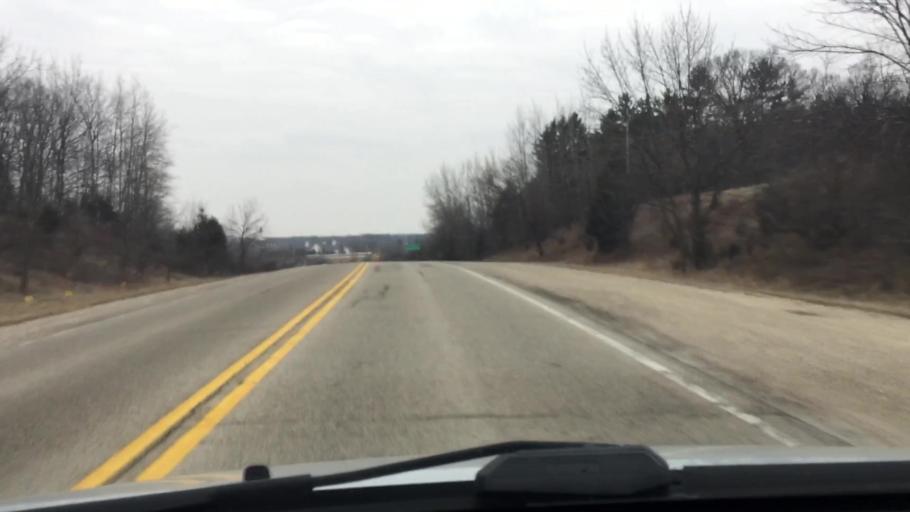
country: US
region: Wisconsin
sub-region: Waukesha County
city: Delafield
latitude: 43.0505
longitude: -88.4044
